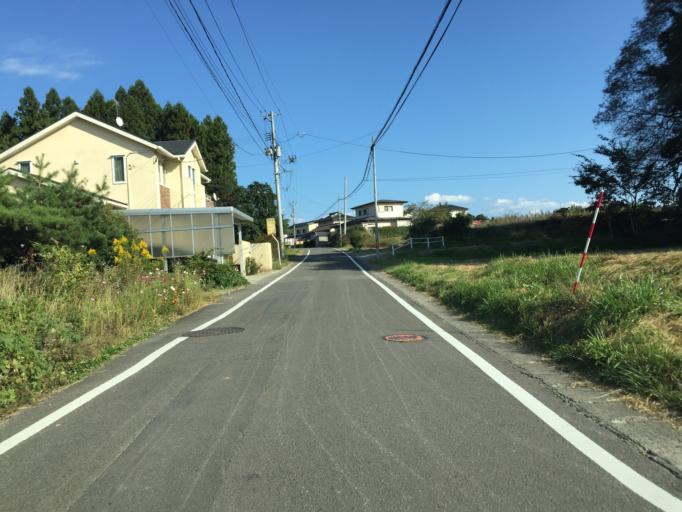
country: JP
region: Fukushima
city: Nihommatsu
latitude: 37.6551
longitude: 140.4697
